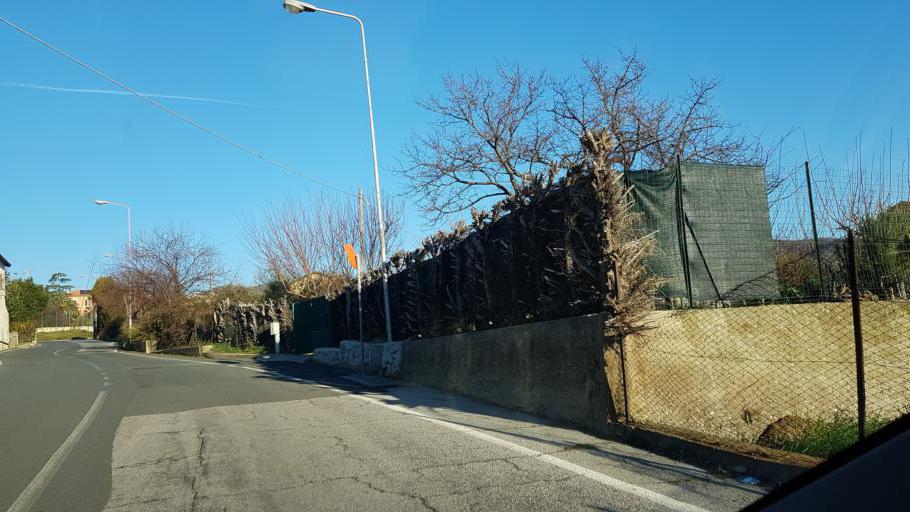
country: IT
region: Liguria
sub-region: Provincia di Savona
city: Valleggia
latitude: 44.2955
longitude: 8.4499
